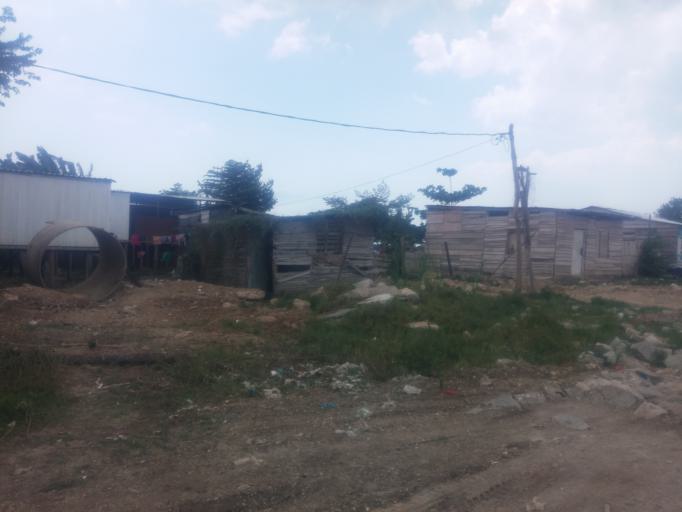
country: CO
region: Bolivar
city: Cartagena
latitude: 10.4159
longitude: -75.4664
